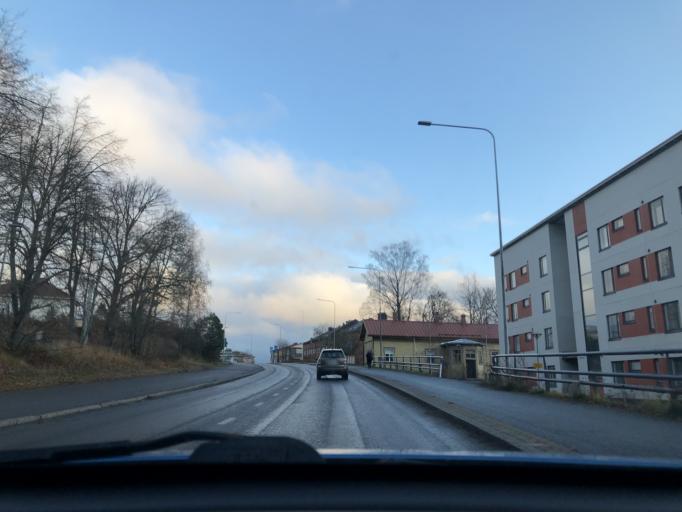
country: FI
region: Pirkanmaa
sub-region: Tampere
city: Kangasala
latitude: 61.4642
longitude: 24.0600
